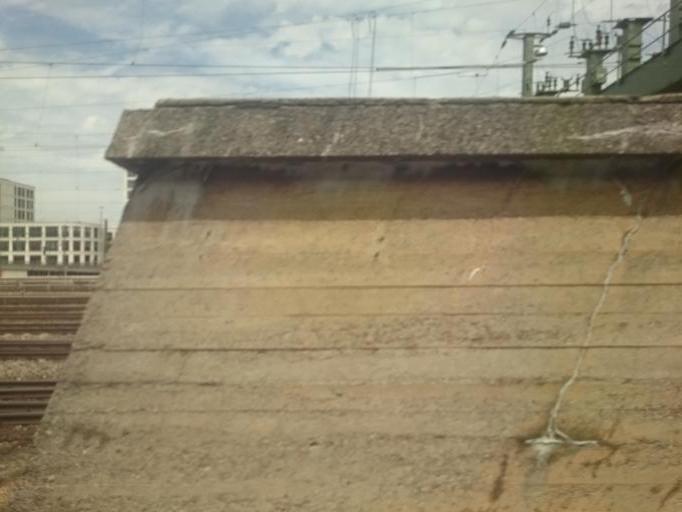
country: DE
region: Bavaria
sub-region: Upper Bavaria
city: Munich
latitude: 48.1413
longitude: 11.5445
